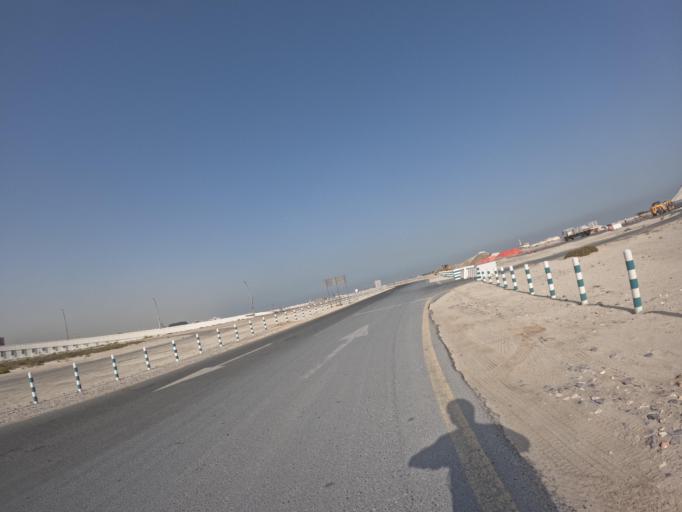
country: AE
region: Dubai
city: Dubai
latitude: 25.1983
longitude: 55.2353
